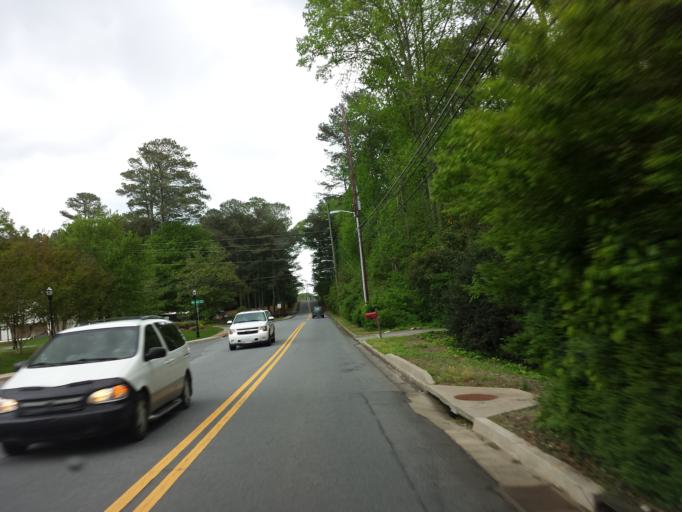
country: US
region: Georgia
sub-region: Cobb County
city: Marietta
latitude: 33.9345
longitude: -84.5639
